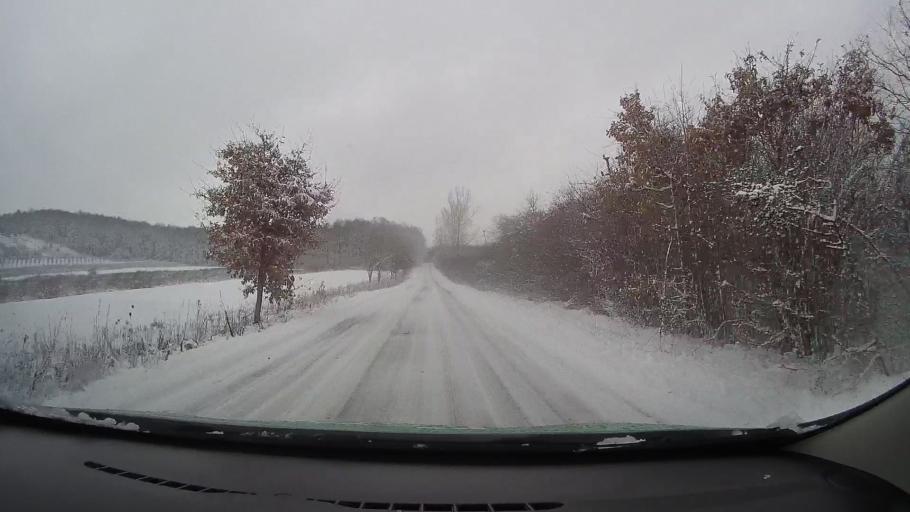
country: RO
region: Hunedoara
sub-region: Comuna Pestisu Mic
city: Pestisu Mic
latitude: 45.8151
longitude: 22.8964
